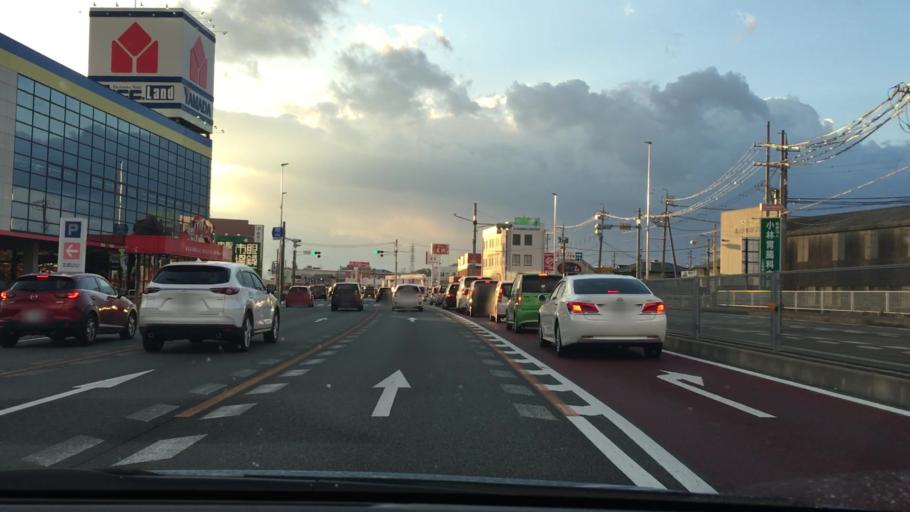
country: JP
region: Mie
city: Ise
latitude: 34.5088
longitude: 136.7220
